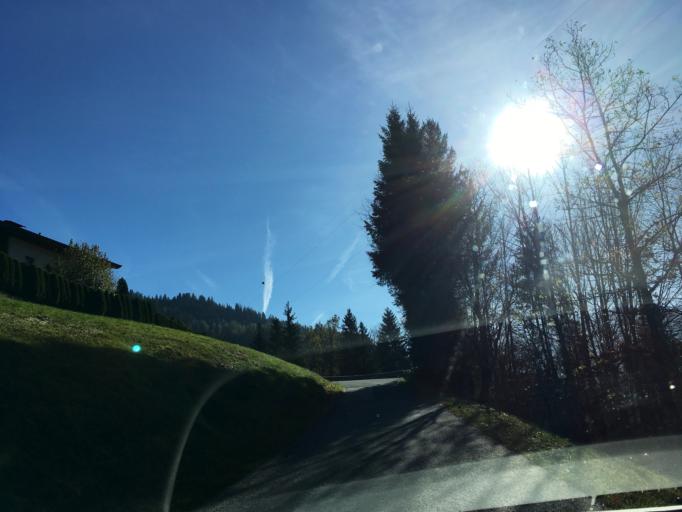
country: AT
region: Tyrol
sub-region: Politischer Bezirk Kufstein
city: Rettenschoss
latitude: 47.6720
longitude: 12.2567
